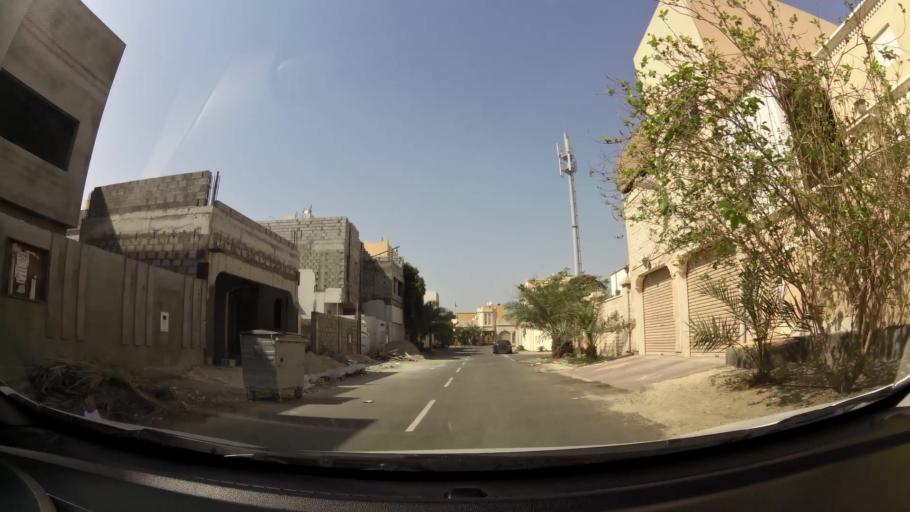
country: BH
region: Manama
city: Jidd Hafs
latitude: 26.2075
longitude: 50.4646
